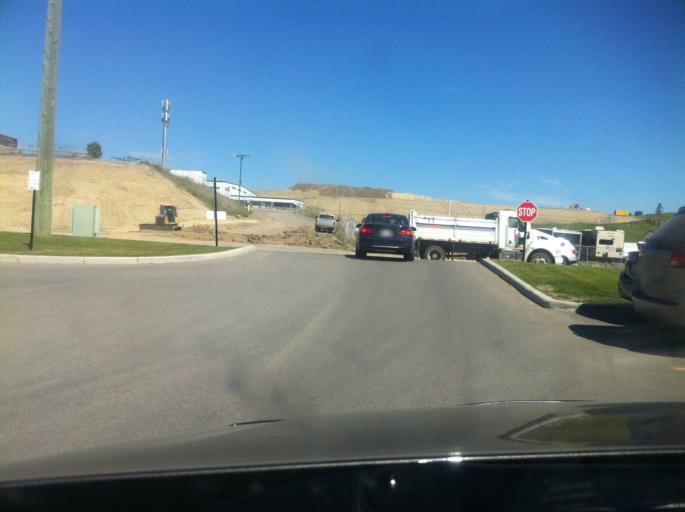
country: CA
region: Alberta
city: Calgary
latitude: 50.9622
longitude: -114.0022
